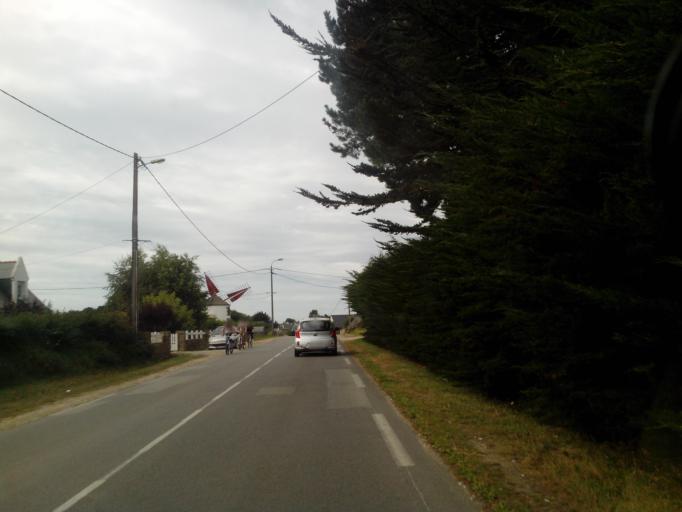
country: FR
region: Brittany
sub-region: Departement du Morbihan
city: Erdeven
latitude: 47.6289
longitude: -3.1589
